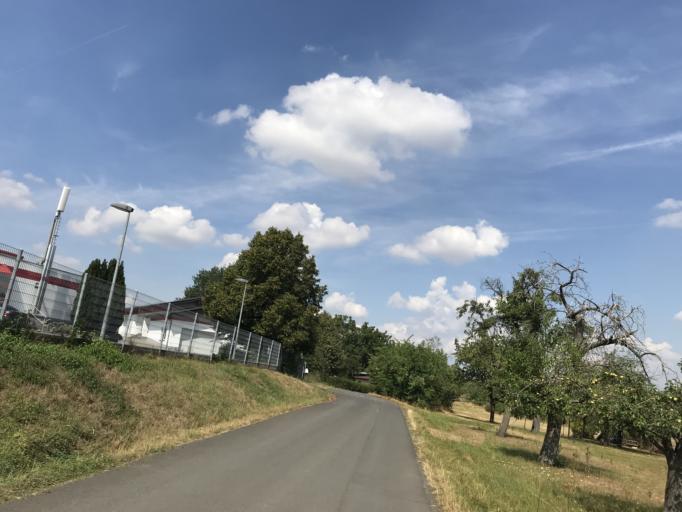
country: DE
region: Hesse
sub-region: Regierungsbezirk Darmstadt
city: Wolfersheim
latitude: 50.4433
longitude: 8.8274
